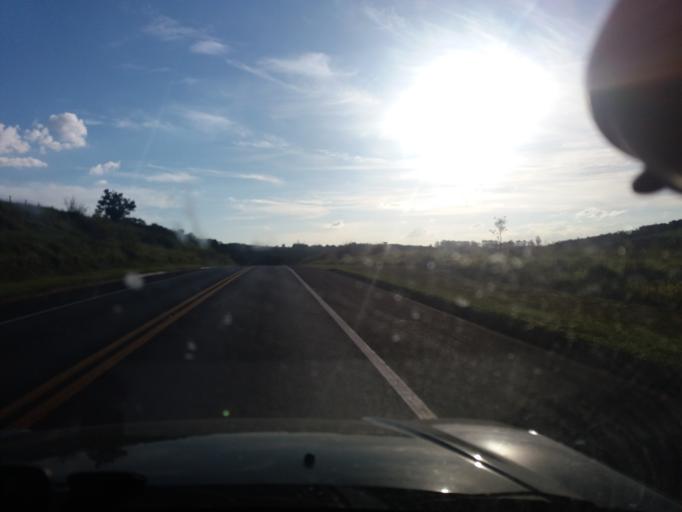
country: BR
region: Sao Paulo
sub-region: Buri
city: Buri
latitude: -23.9290
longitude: -48.6517
